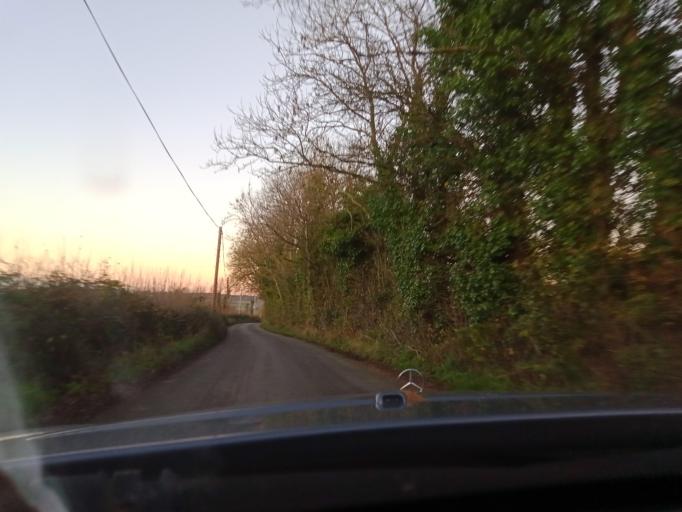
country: IE
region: Leinster
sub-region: Kilkenny
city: Thomastown
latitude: 52.4821
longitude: -7.1009
